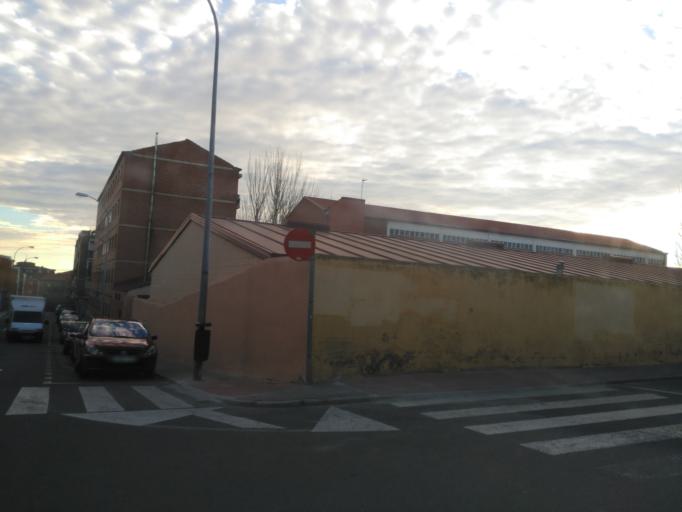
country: ES
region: Castille and Leon
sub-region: Provincia de Salamanca
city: Salamanca
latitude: 40.9773
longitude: -5.6719
